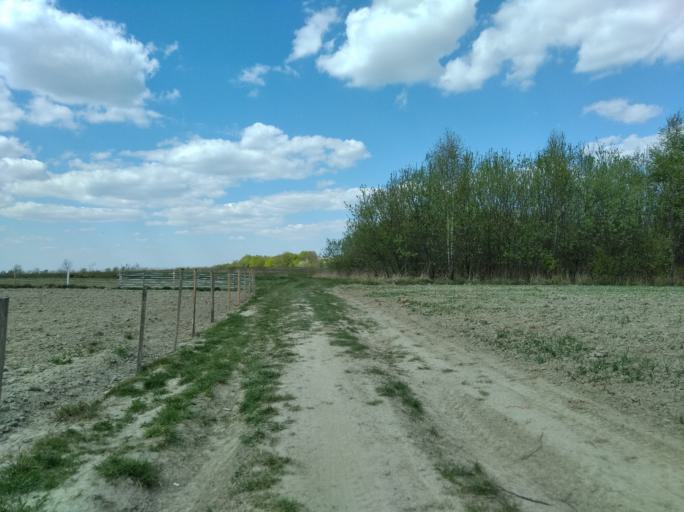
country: PL
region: Subcarpathian Voivodeship
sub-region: Powiat brzozowski
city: Golcowa
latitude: 49.7544
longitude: 22.0733
